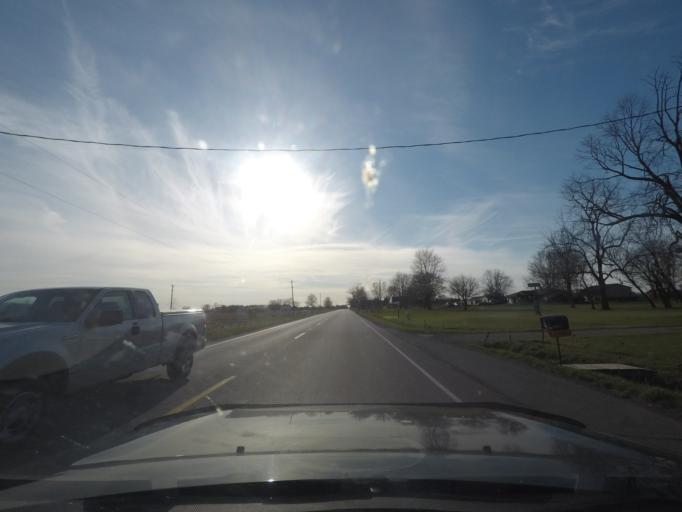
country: US
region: Indiana
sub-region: Marshall County
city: Plymouth
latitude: 41.4495
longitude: -86.2639
